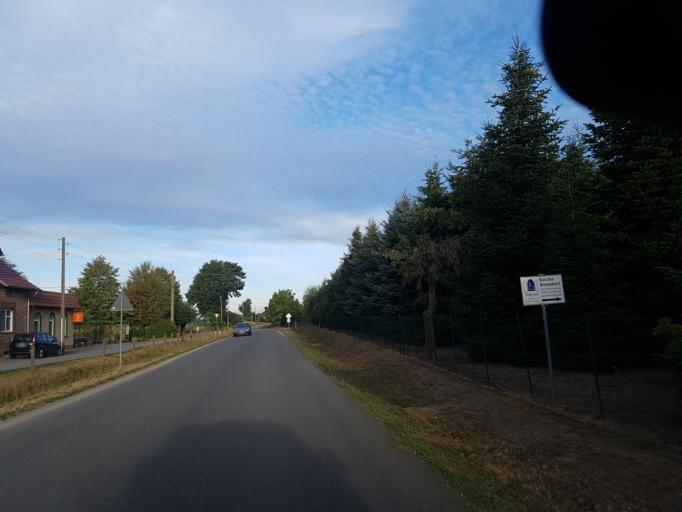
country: DE
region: Brandenburg
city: Dahme
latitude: 51.8603
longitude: 13.3827
